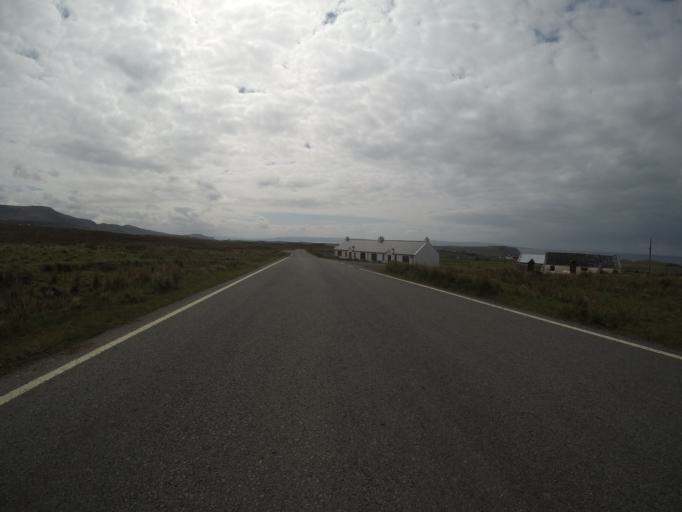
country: GB
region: Scotland
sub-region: Highland
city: Portree
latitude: 57.6592
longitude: -6.3732
